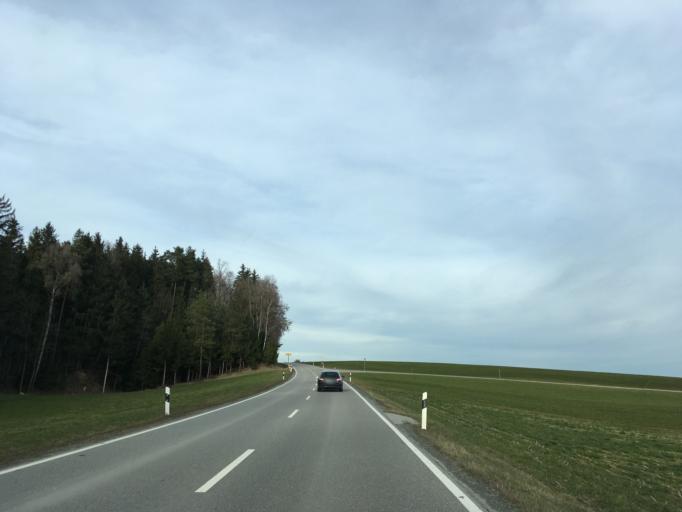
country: DE
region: Bavaria
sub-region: Upper Bavaria
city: Vogtareuth
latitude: 47.9528
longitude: 12.2032
